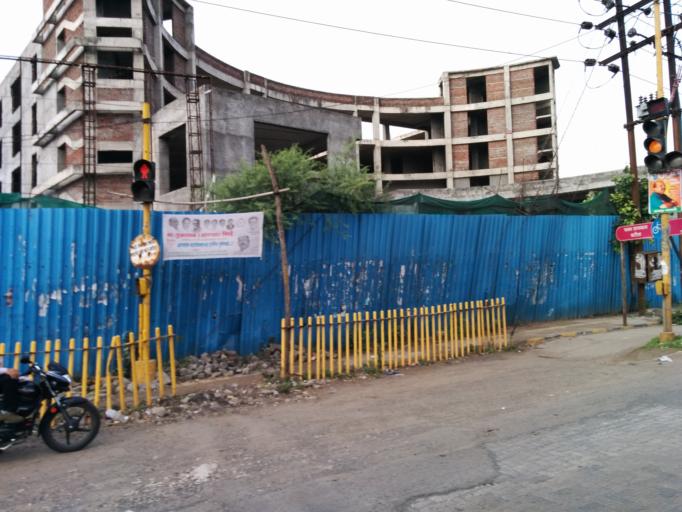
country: IN
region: Maharashtra
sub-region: Pune Division
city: Pune
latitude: 18.5064
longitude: 73.9068
